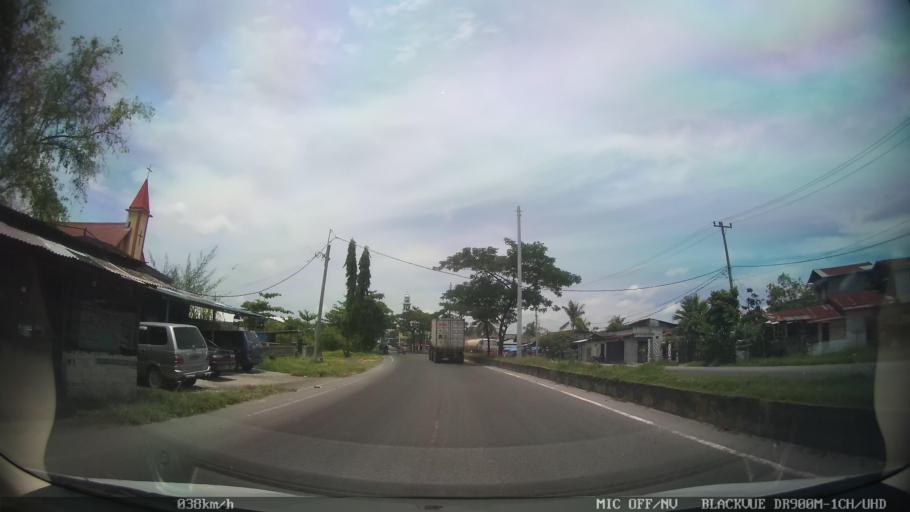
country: ID
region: North Sumatra
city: Belawan
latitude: 3.7717
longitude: 98.6840
